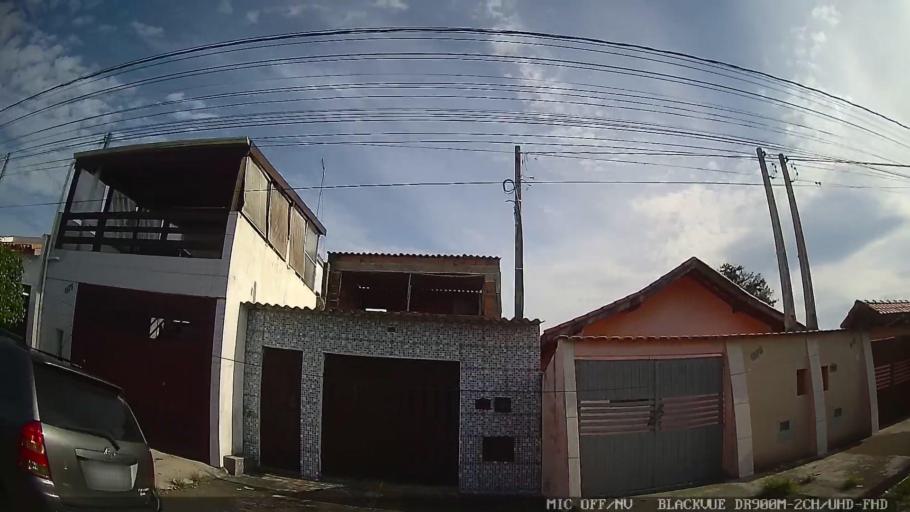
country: BR
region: Sao Paulo
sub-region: Itanhaem
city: Itanhaem
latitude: -24.1547
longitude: -46.7755
